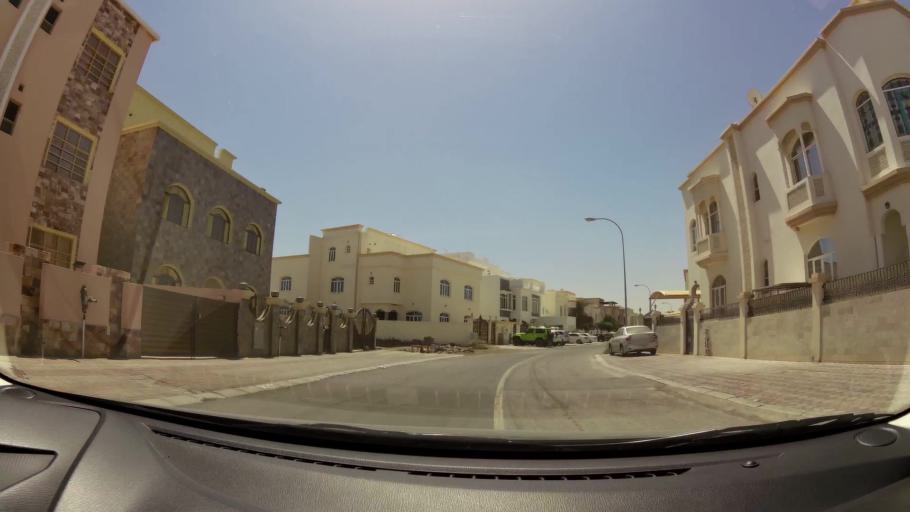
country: OM
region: Muhafazat Masqat
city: As Sib al Jadidah
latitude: 23.6271
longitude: 58.2500
